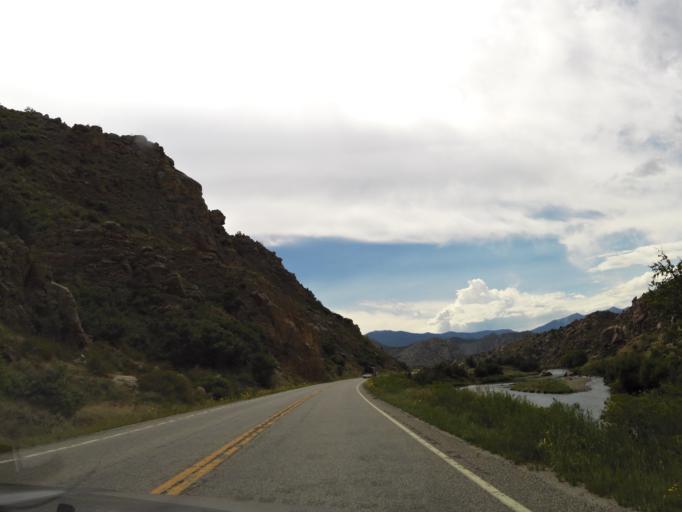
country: US
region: Colorado
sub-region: Custer County
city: Westcliffe
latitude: 38.3863
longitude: -105.6579
